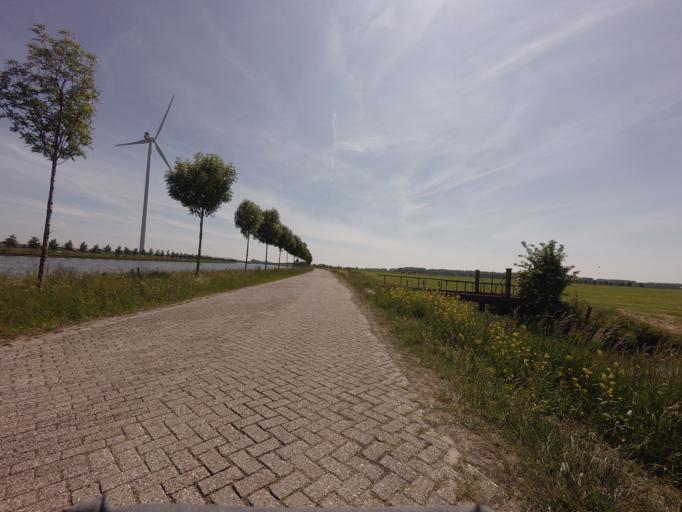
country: NL
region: Utrecht
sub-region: Gemeente Houten
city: Houten
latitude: 52.0144
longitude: 5.1469
